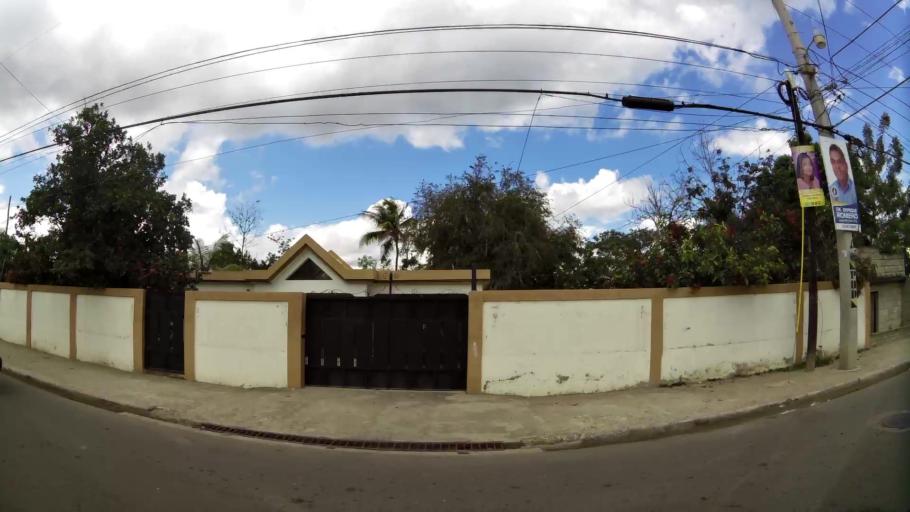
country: DO
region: Santiago
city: Licey al Medio
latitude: 19.4016
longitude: -70.6542
